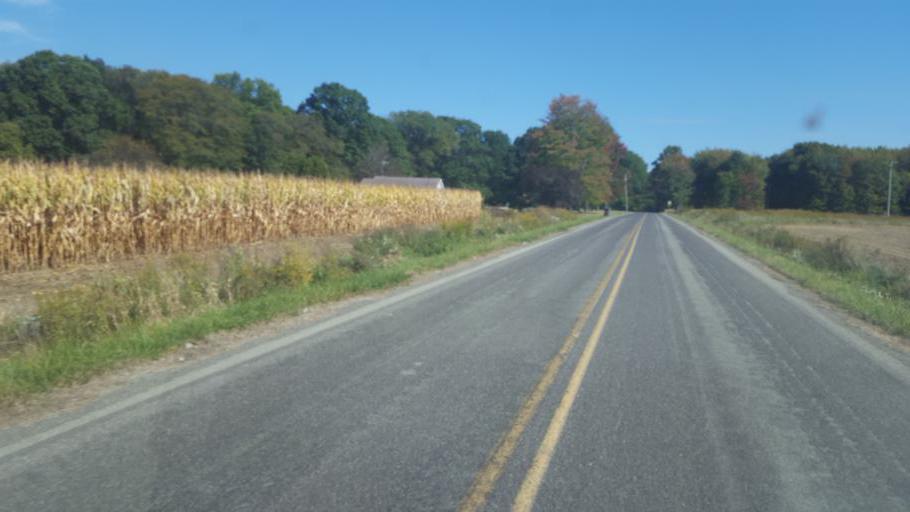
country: US
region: Pennsylvania
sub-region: Mercer County
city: Reynolds Heights
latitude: 41.3673
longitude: -80.3760
